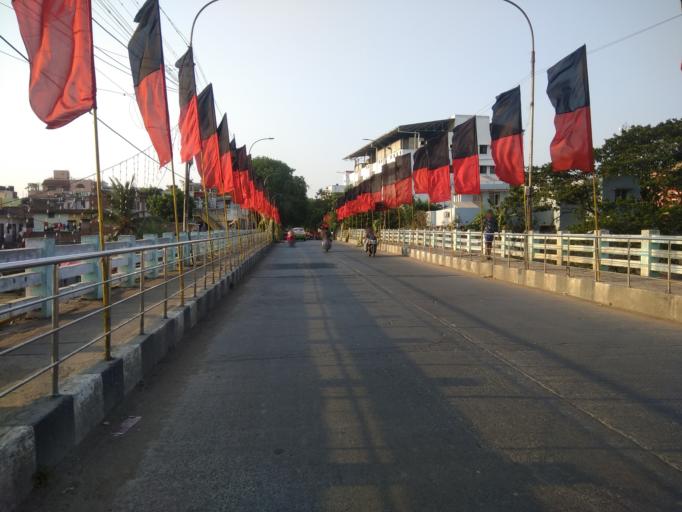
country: IN
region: Tamil Nadu
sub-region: Chennai
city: Chetput
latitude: 13.0778
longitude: 80.2119
